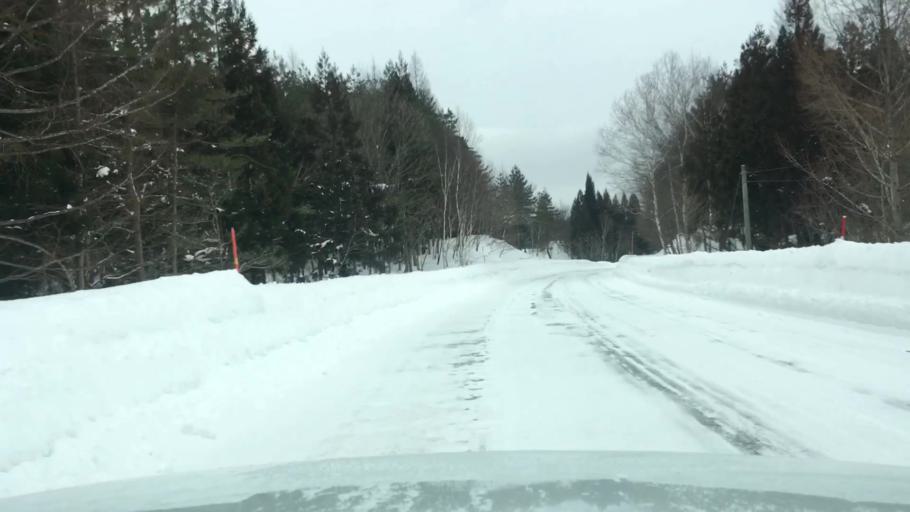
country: JP
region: Akita
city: Hanawa
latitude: 39.9893
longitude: 140.9969
